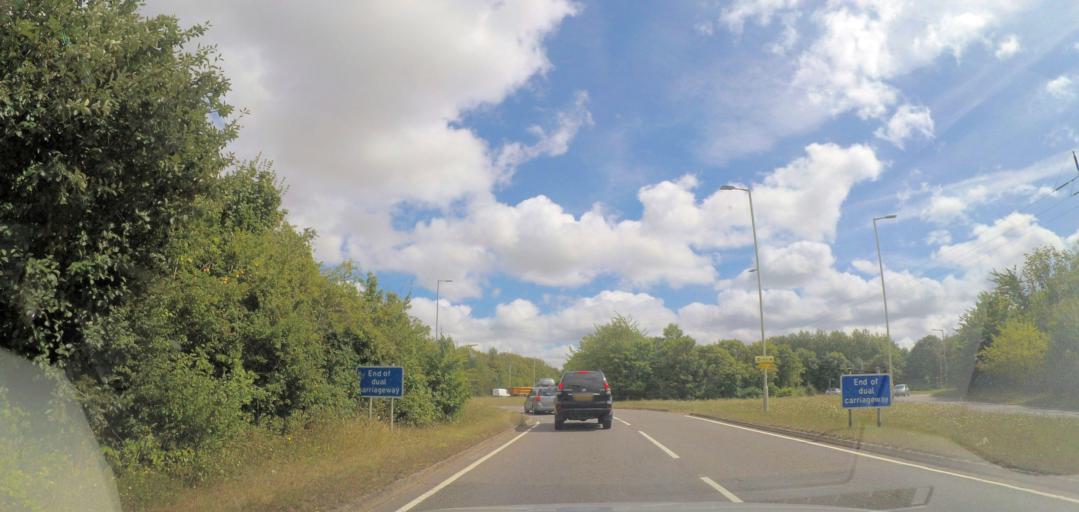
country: GB
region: England
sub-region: Hertfordshire
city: Royston
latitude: 52.0616
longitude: -0.0138
